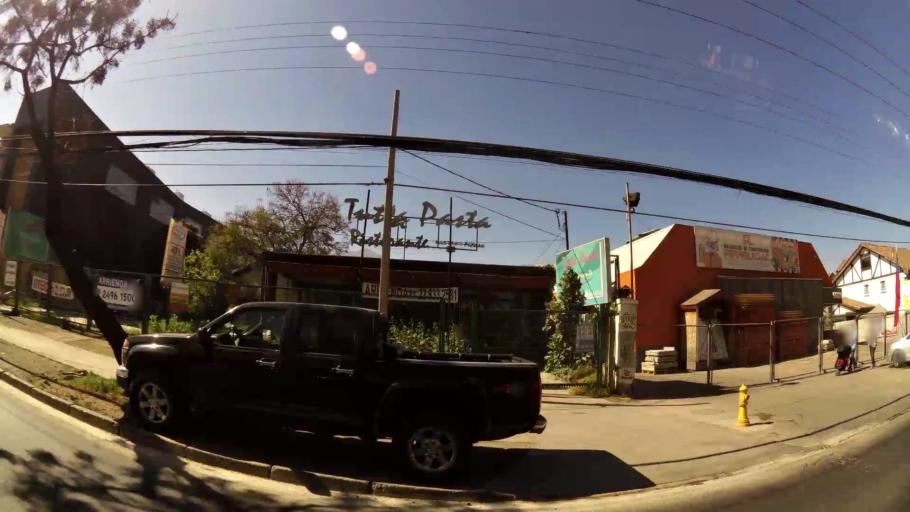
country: CL
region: Santiago Metropolitan
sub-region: Provincia de Santiago
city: Villa Presidente Frei, Nunoa, Santiago, Chile
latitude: -33.3874
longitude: -70.5386
